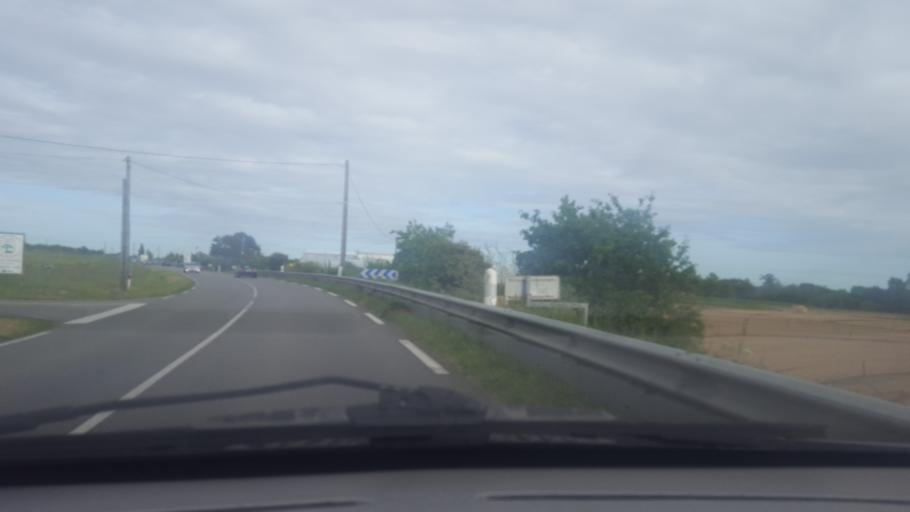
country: FR
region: Pays de la Loire
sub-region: Departement de la Loire-Atlantique
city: Bourgneuf-en-Retz
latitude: 47.0331
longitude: -1.9276
